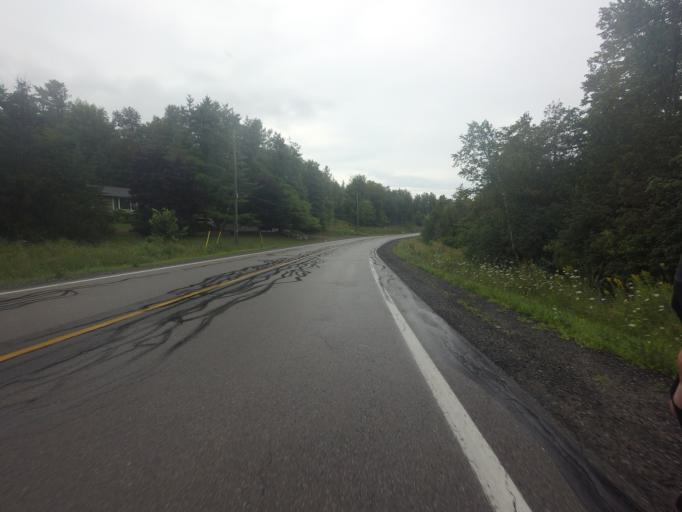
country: CA
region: Ontario
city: Perth
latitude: 45.0072
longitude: -76.3705
